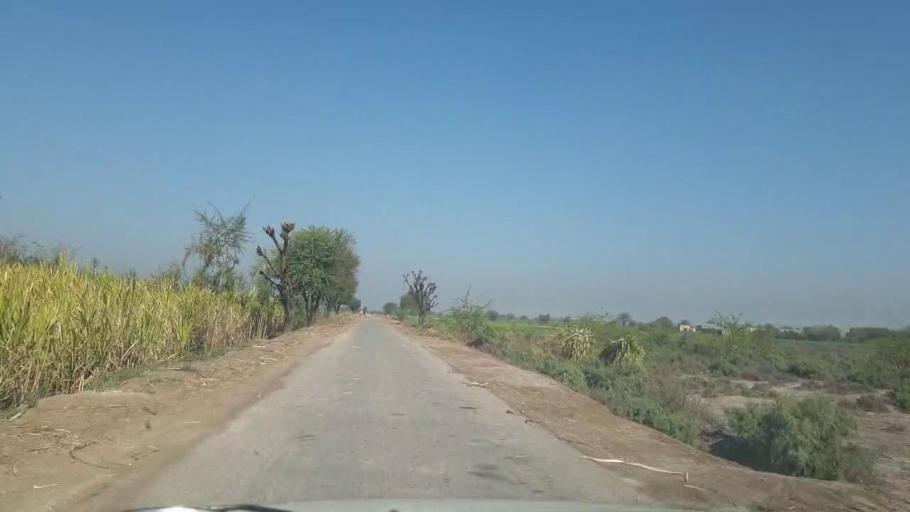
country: PK
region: Sindh
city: Mirpur Khas
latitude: 25.4978
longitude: 69.1743
